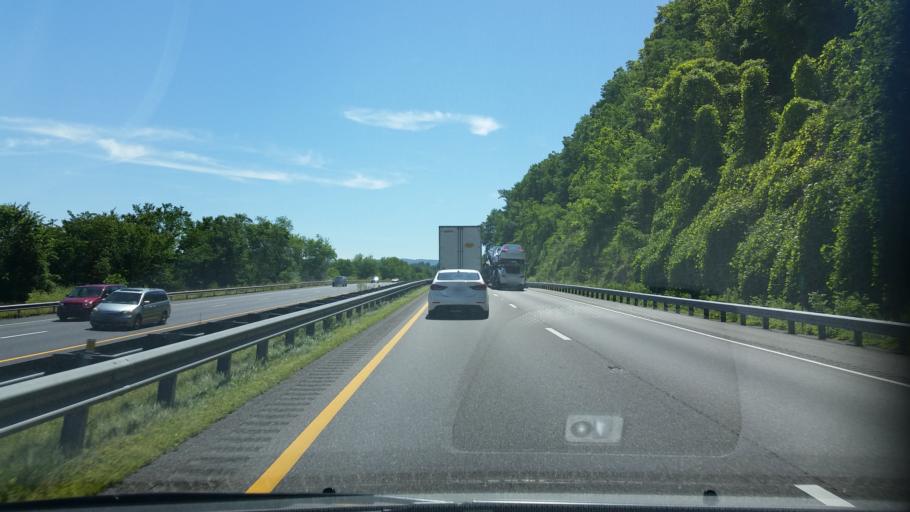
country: US
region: Virginia
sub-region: Smyth County
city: Chilhowie
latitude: 36.8081
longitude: -81.6388
